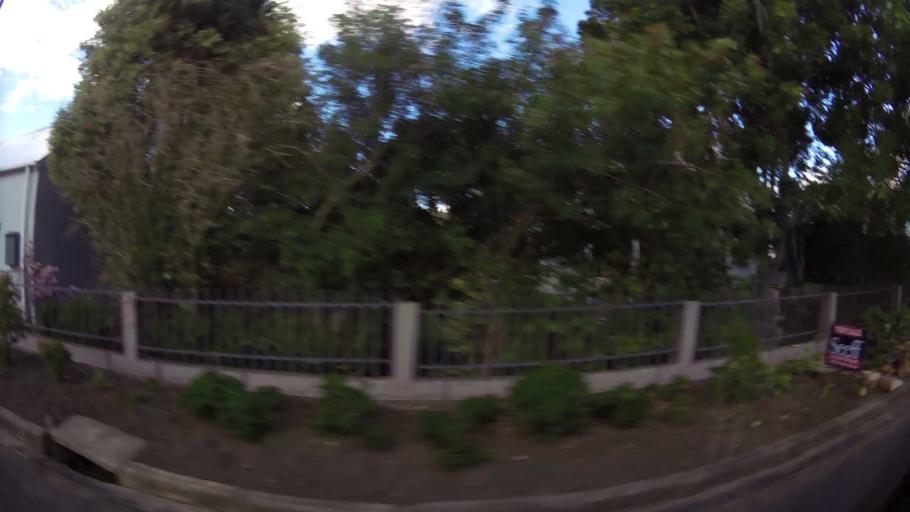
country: ZA
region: Western Cape
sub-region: Overberg District Municipality
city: Swellendam
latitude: -34.0117
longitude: 20.4559
